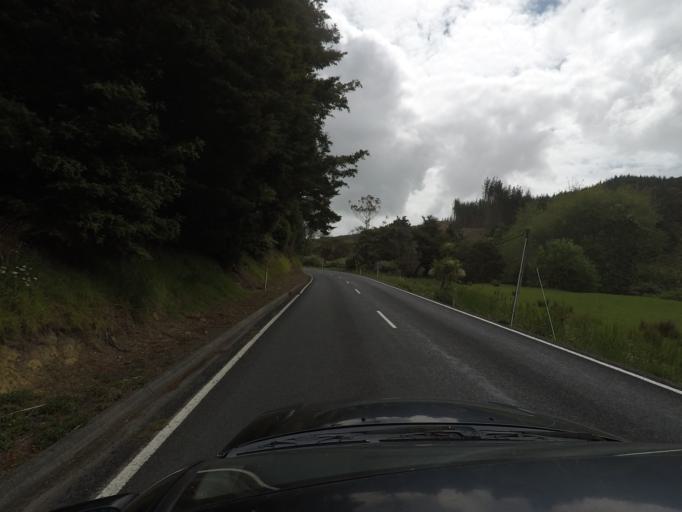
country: NZ
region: Auckland
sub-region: Auckland
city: Parakai
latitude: -36.5025
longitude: 174.4717
